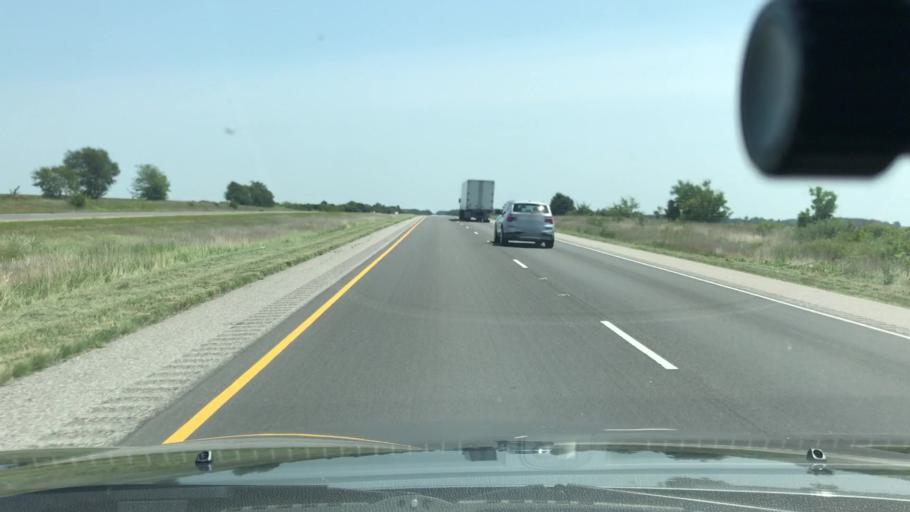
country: US
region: Illinois
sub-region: Washington County
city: Nashville
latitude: 38.3902
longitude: -89.2471
